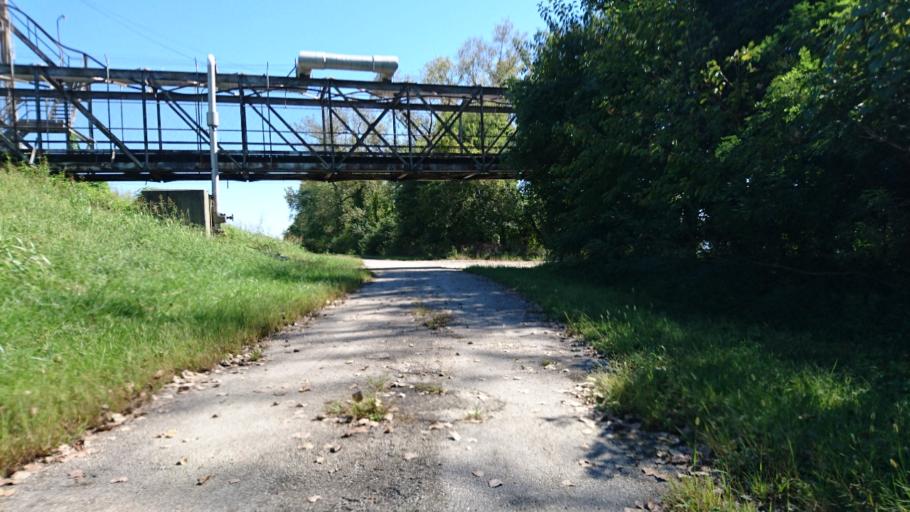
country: US
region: Illinois
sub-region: Madison County
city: East Alton
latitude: 38.8634
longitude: -90.1356
